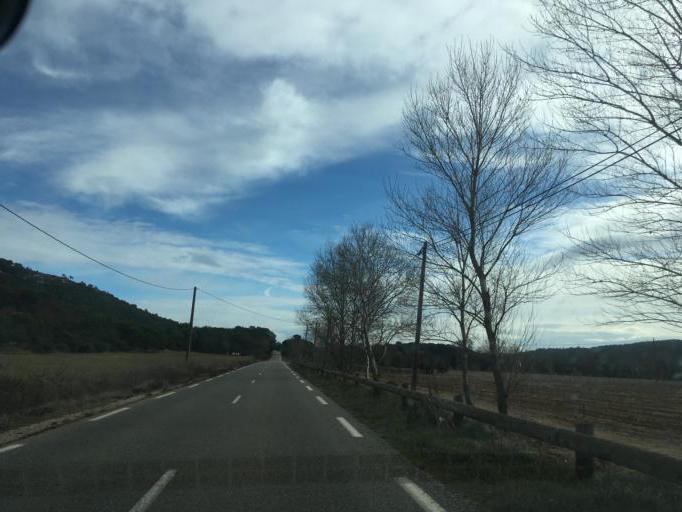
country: FR
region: Provence-Alpes-Cote d'Azur
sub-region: Departement du Var
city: Bras
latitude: 43.4458
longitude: 6.0079
